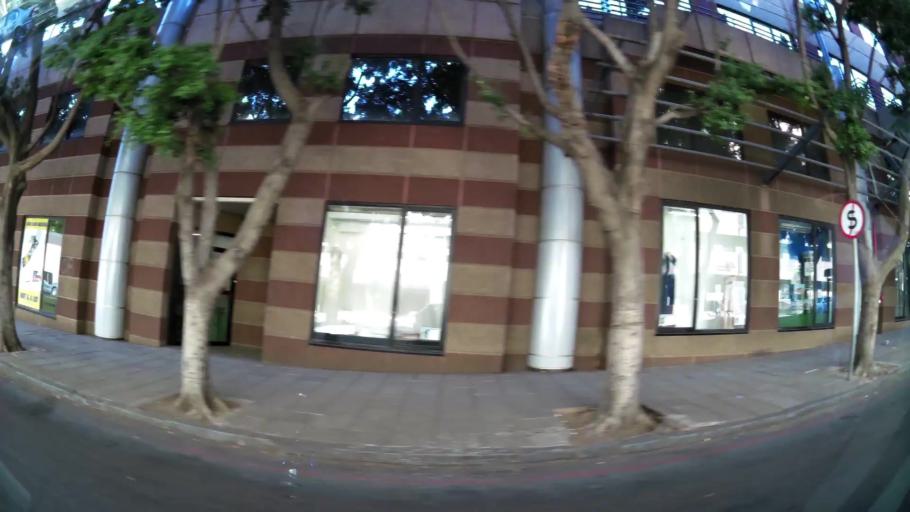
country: ZA
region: Gauteng
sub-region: City of Tshwane Metropolitan Municipality
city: Pretoria
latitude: -25.7453
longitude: 28.2046
